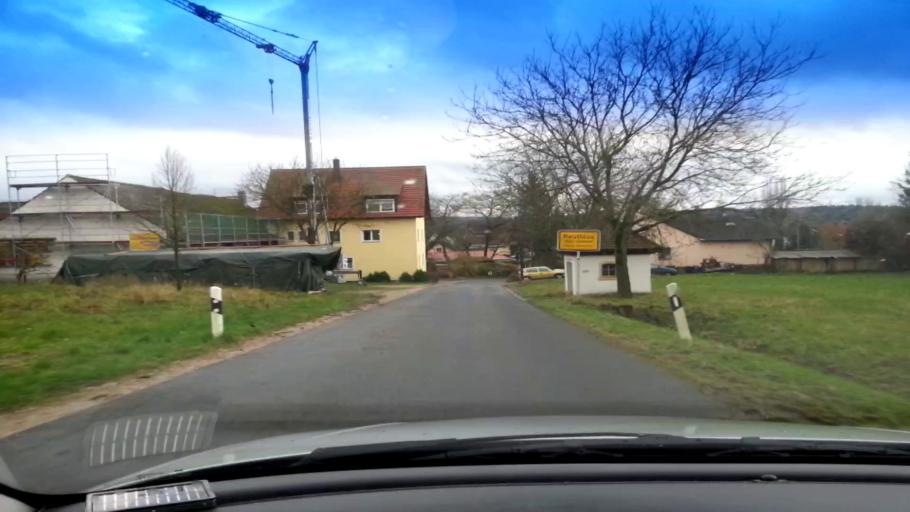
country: DE
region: Bavaria
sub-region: Upper Franconia
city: Zapfendorf
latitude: 50.0230
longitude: 10.9691
